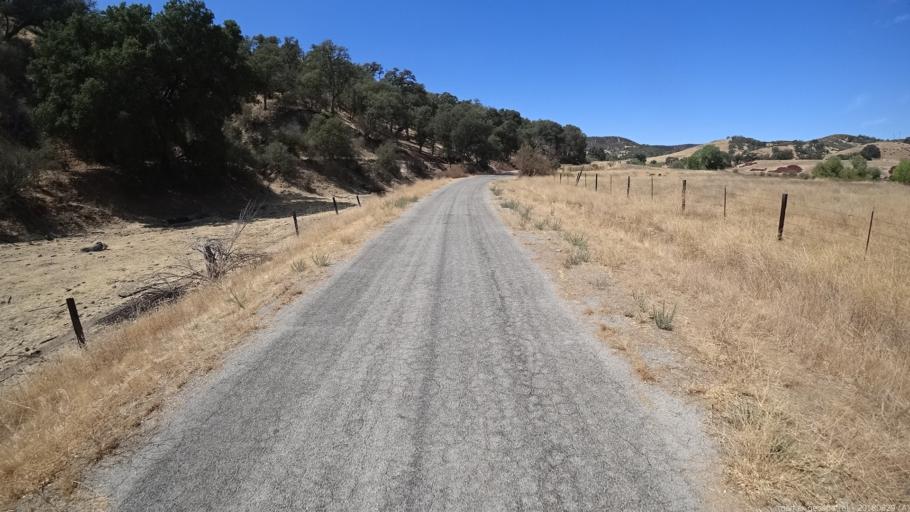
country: US
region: California
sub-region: San Luis Obispo County
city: Lake Nacimiento
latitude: 35.8624
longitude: -121.0278
